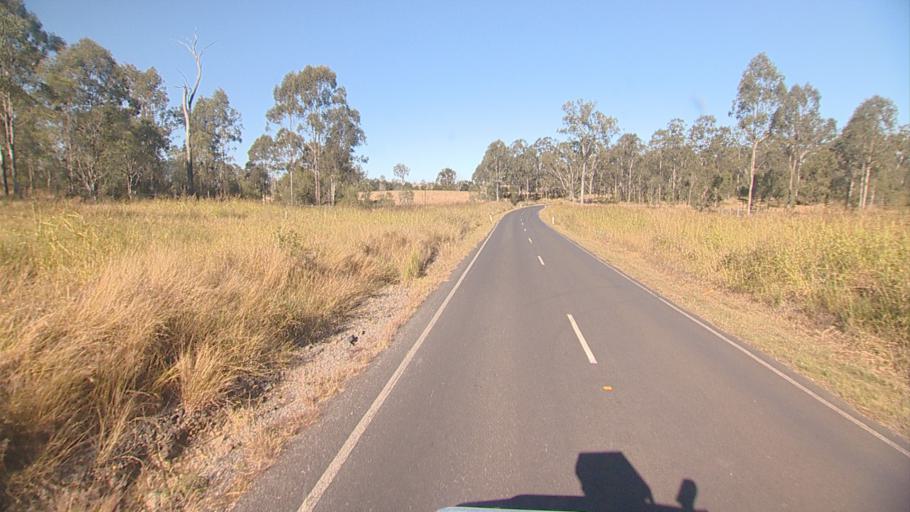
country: AU
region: Queensland
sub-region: Logan
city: North Maclean
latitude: -27.8362
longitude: 152.9374
